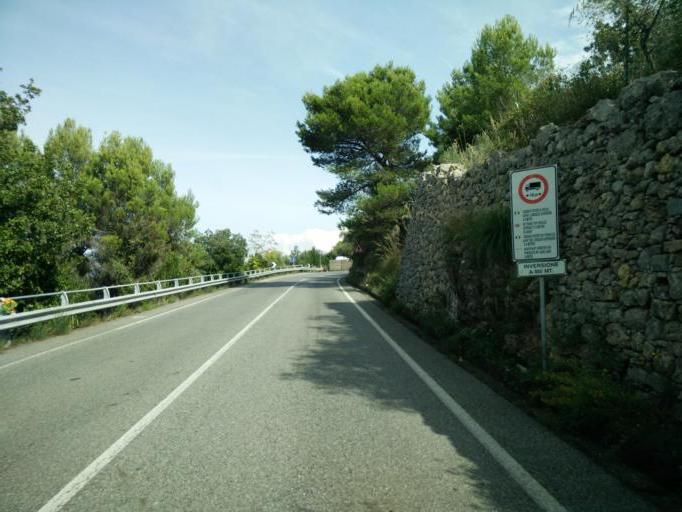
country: IT
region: Liguria
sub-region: Provincia di La Spezia
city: Le Grazie
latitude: 44.0617
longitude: 9.8417
